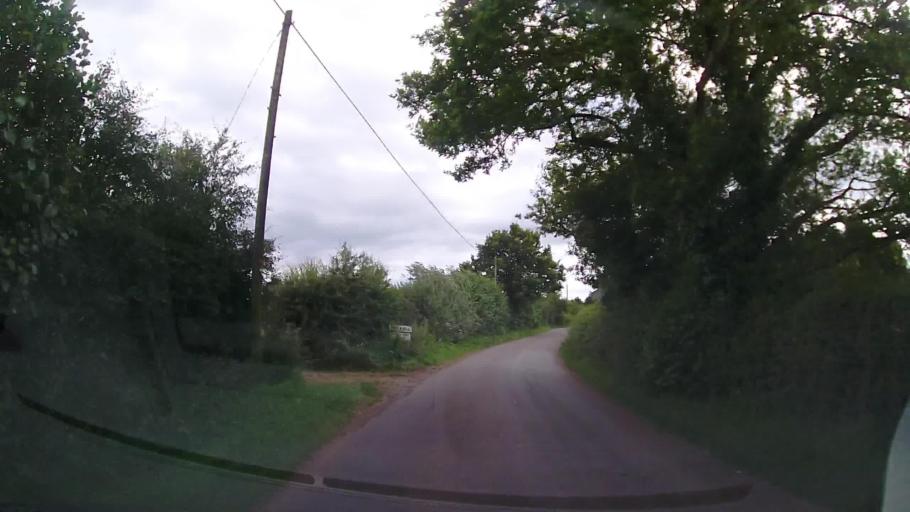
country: GB
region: England
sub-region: Shropshire
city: Whitchurch
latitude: 52.9252
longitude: -2.7238
